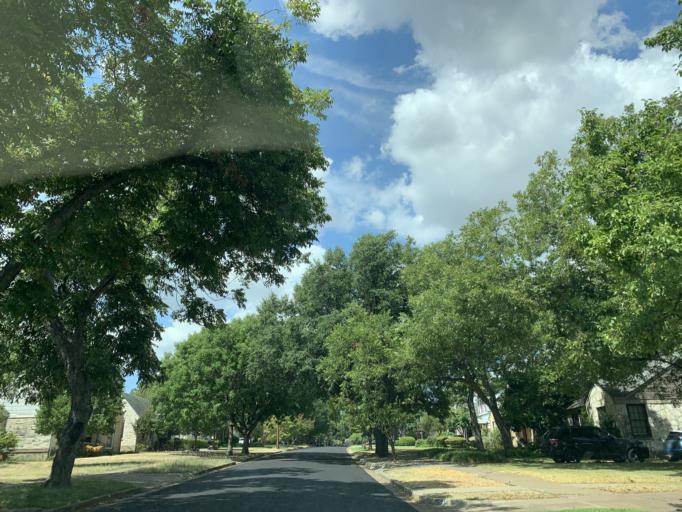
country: US
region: Texas
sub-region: Dallas County
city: Cockrell Hill
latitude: 32.7451
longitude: -96.8592
